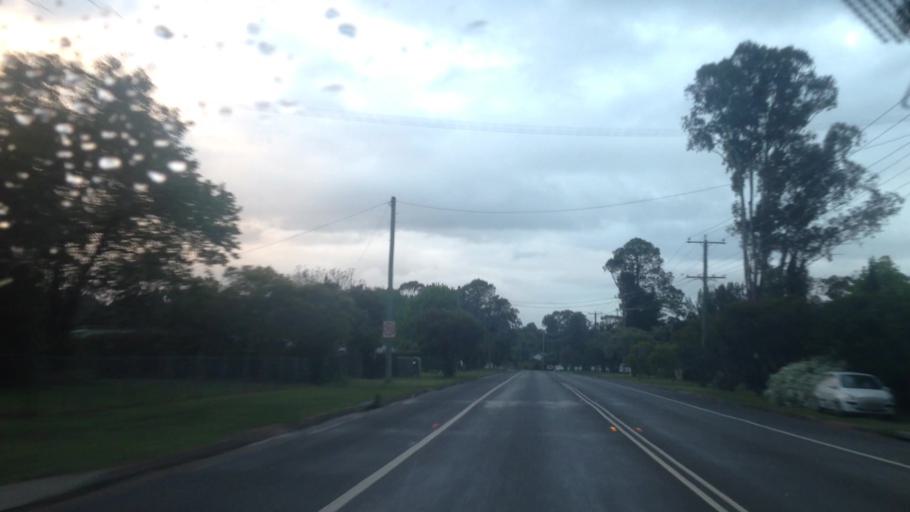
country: AU
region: New South Wales
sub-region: Lake Macquarie Shire
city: Cooranbong
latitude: -33.0832
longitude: 151.4477
